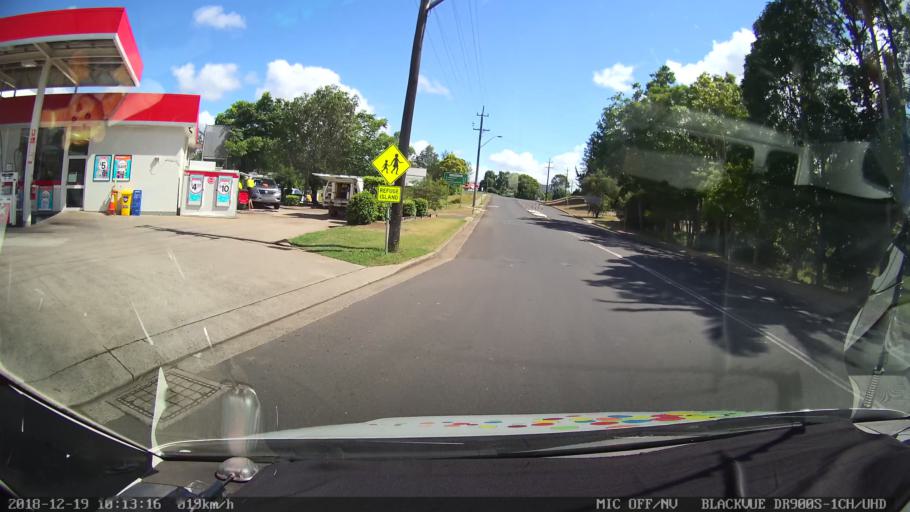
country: AU
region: New South Wales
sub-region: Kyogle
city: Kyogle
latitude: -28.6182
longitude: 153.0039
